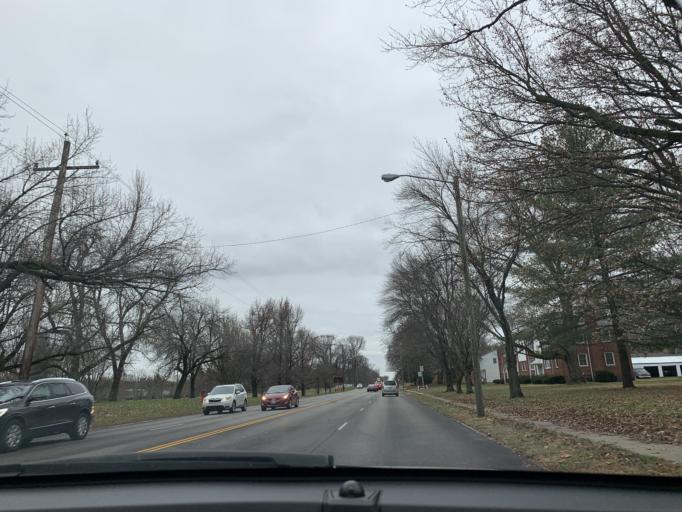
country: US
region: Illinois
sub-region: Sangamon County
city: Leland Grove
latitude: 39.7925
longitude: -89.6871
